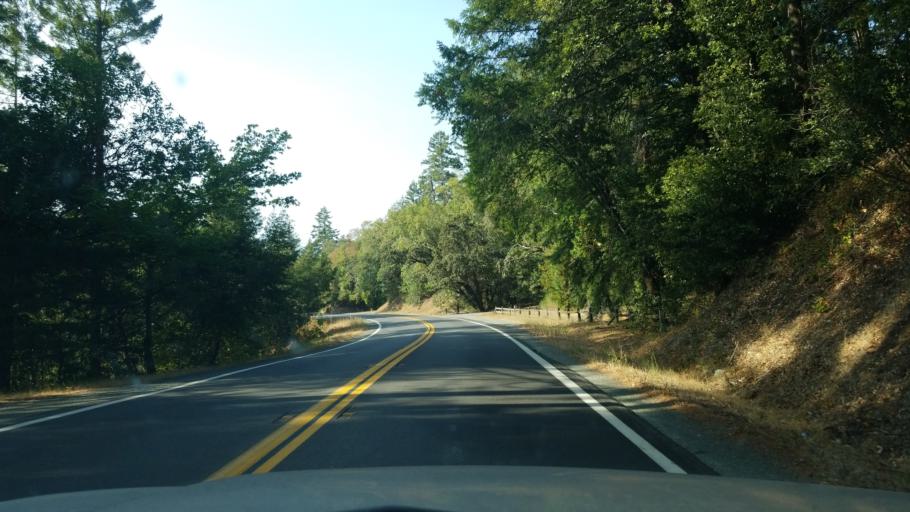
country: US
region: California
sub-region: Humboldt County
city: Redway
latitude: 40.2218
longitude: -123.8199
